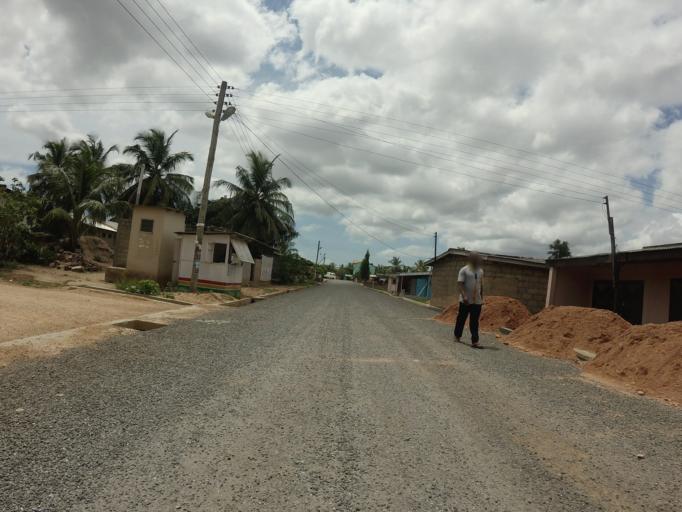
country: GH
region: Central
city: Kasoa
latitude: 5.5475
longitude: -0.3991
